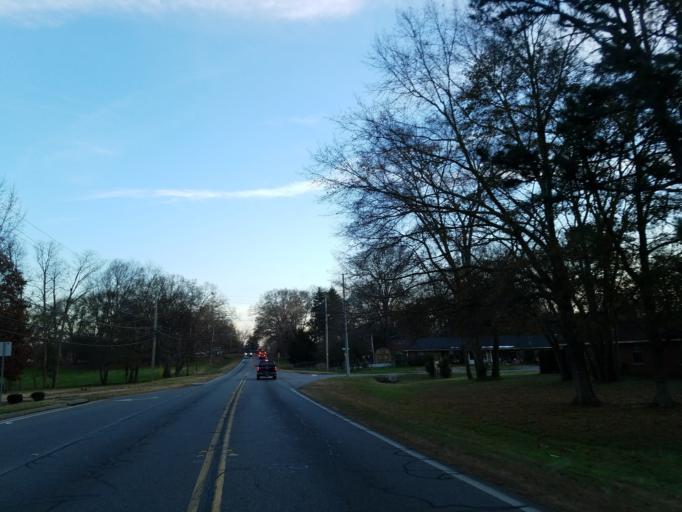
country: US
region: Georgia
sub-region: Bartow County
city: Cartersville
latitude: 34.1874
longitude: -84.8176
